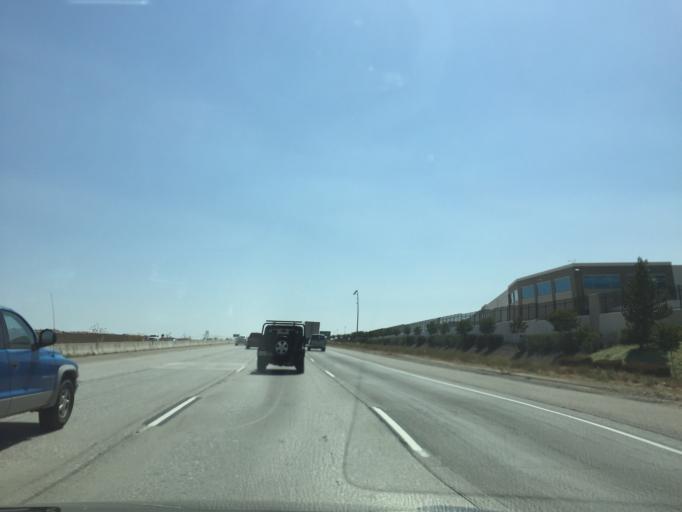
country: US
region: California
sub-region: San Bernardino County
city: Muscoy
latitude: 34.1914
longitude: -117.4246
